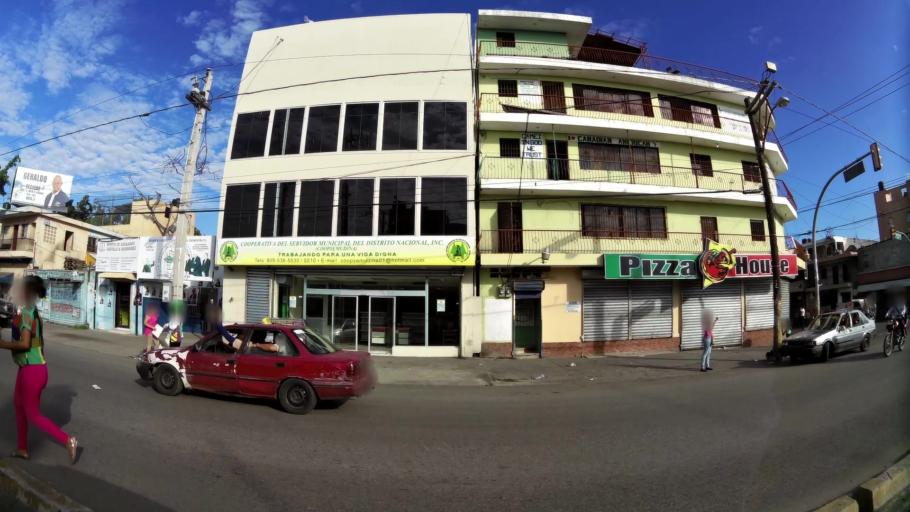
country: DO
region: Nacional
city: Ensanche Luperon
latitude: 18.4984
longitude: -69.8922
